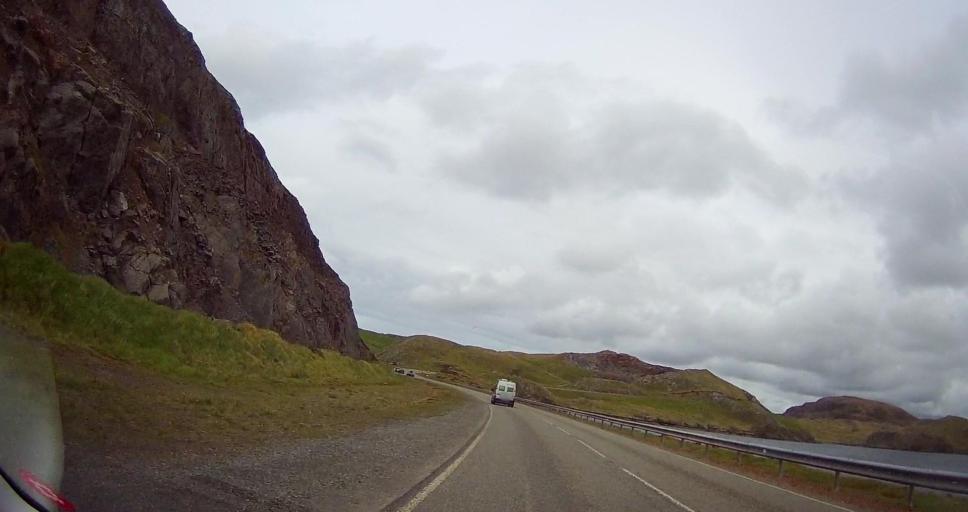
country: GB
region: Scotland
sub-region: Shetland Islands
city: Lerwick
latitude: 60.3957
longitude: -1.3796
